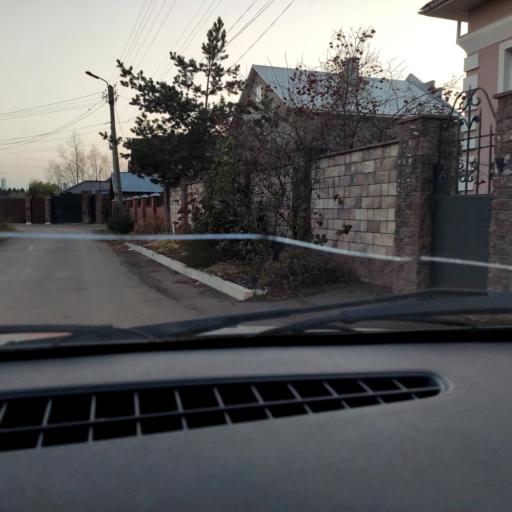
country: RU
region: Bashkortostan
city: Ufa
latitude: 54.7699
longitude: 55.9459
